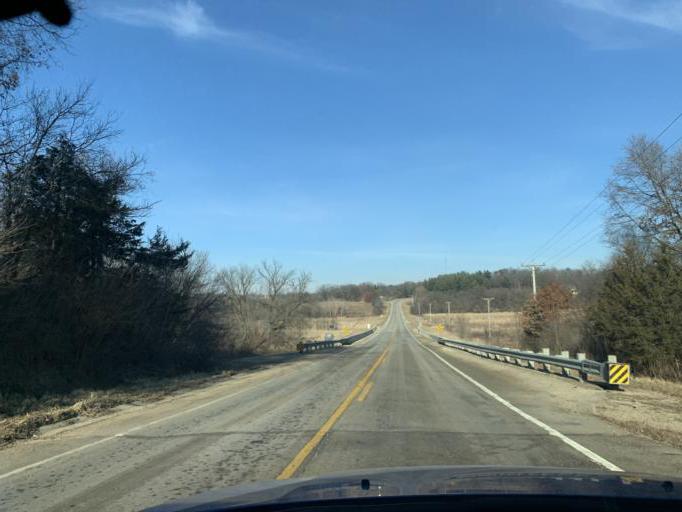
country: US
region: Wisconsin
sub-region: Green County
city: New Glarus
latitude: 42.7849
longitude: -89.8612
